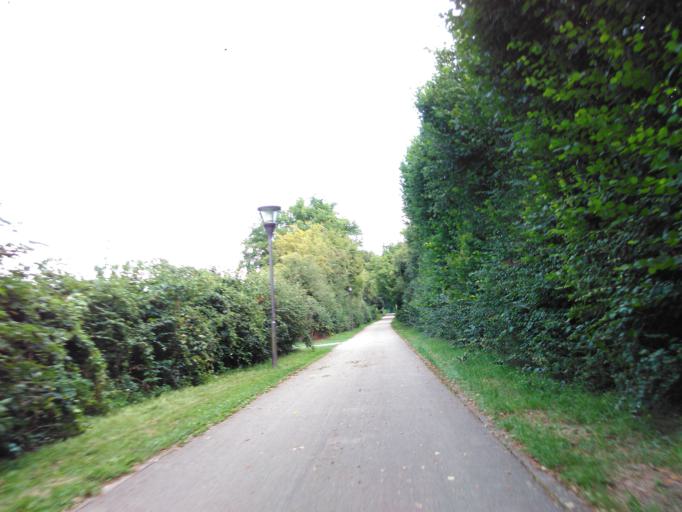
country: DE
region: Rheinland-Pfalz
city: Minden
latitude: 49.8185
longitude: 6.4737
